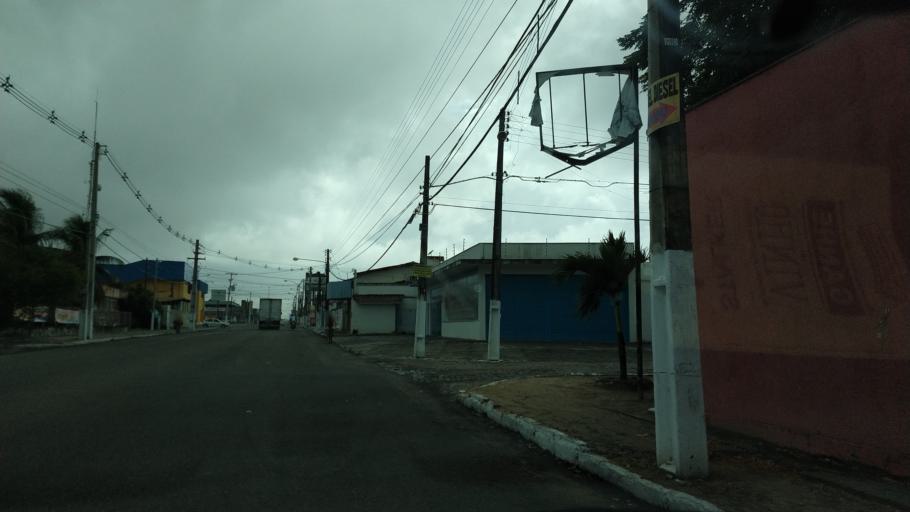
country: BR
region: Rio Grande do Norte
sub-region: Parnamirim
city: Parnamirim
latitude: -5.9231
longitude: -35.2701
